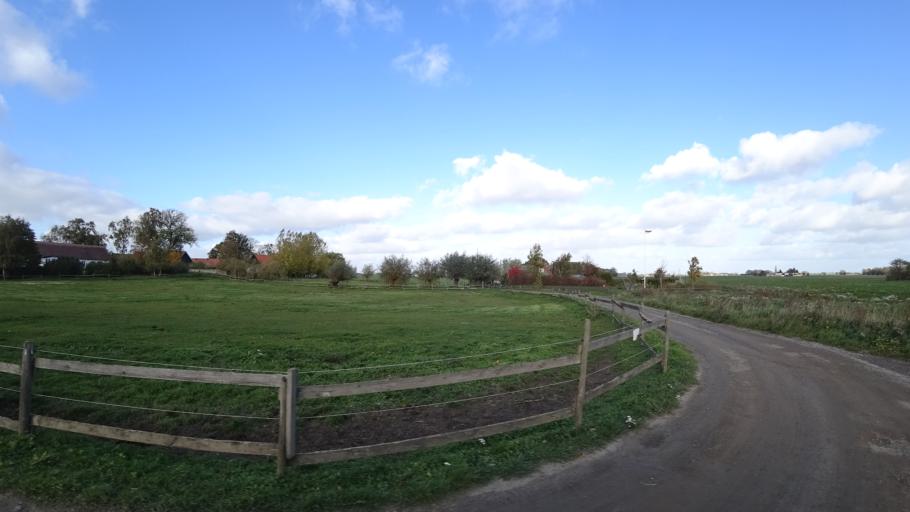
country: SE
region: Skane
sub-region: Staffanstorps Kommun
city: Hjaerup
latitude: 55.6442
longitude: 13.1388
